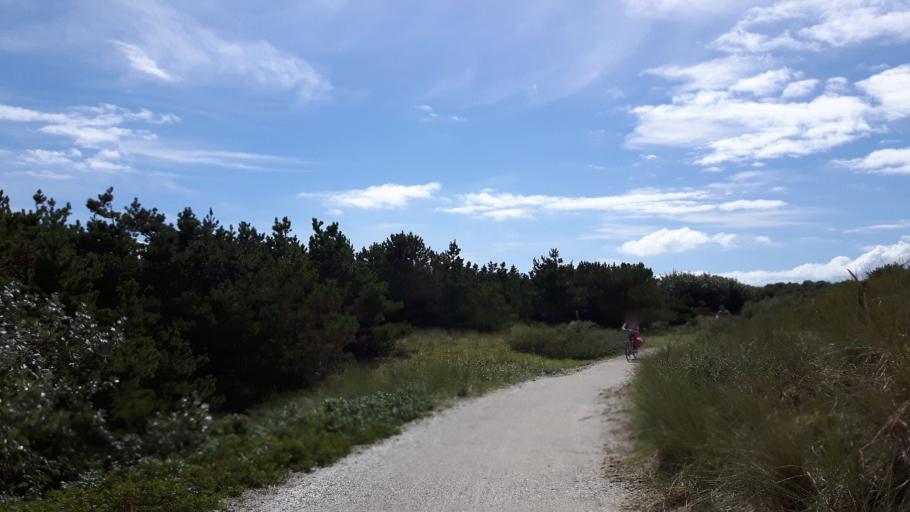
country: NL
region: Friesland
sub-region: Gemeente Ameland
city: Hollum
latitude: 53.4474
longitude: 5.6175
